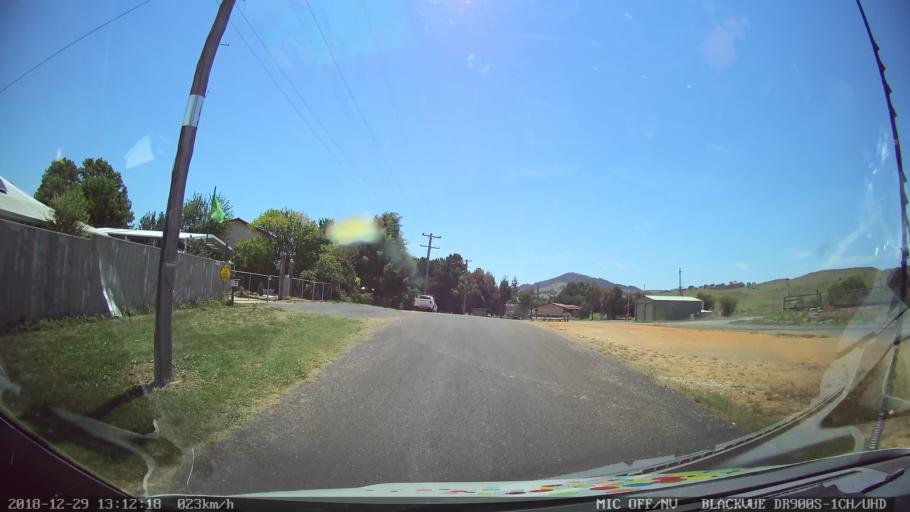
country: AU
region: Australian Capital Territory
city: Macarthur
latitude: -35.7103
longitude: 149.1653
